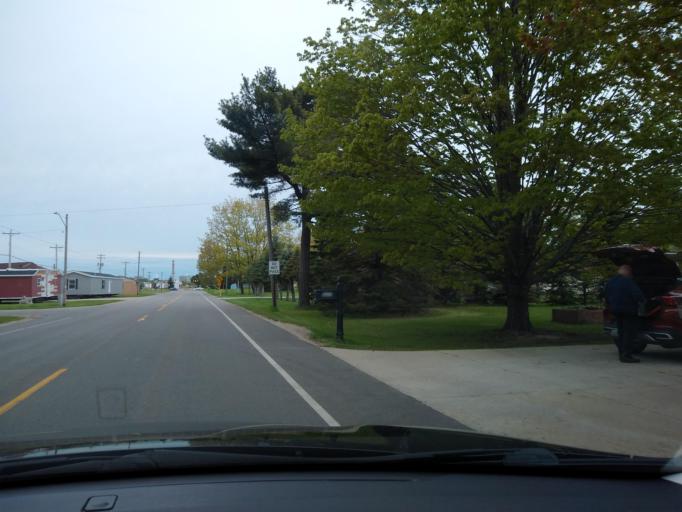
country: US
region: Michigan
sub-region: Delta County
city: Escanaba
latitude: 45.7875
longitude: -87.0791
